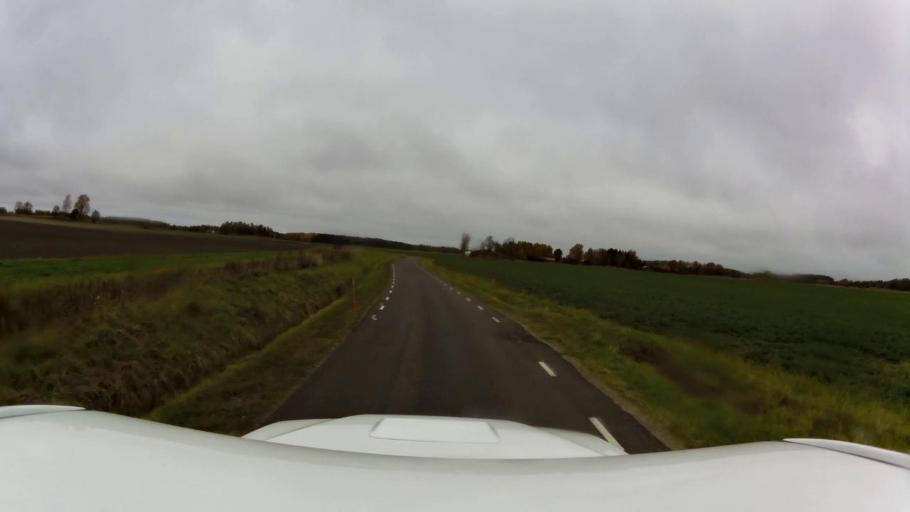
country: SE
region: OEstergoetland
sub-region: Linkopings Kommun
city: Linghem
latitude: 58.4816
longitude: 15.8162
